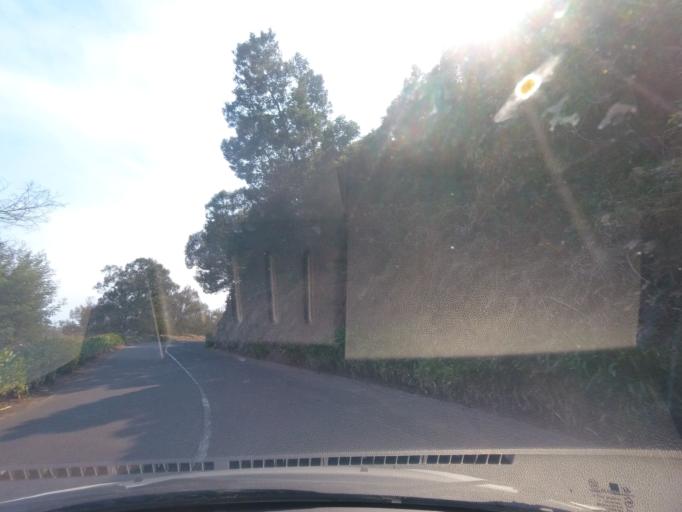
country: PT
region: Madeira
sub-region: Ribeira Brava
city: Campanario
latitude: 32.6906
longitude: -17.0606
